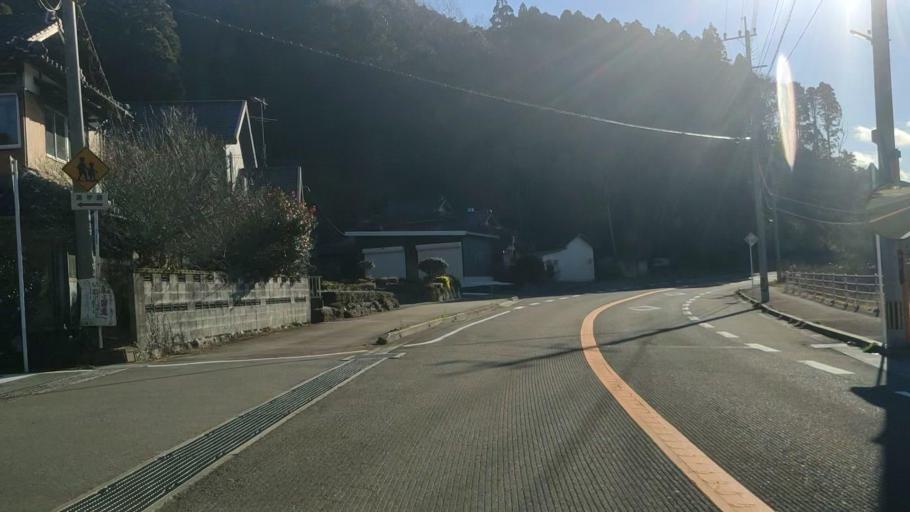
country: JP
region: Fukuoka
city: Maebaru-chuo
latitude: 33.4423
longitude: 130.2688
